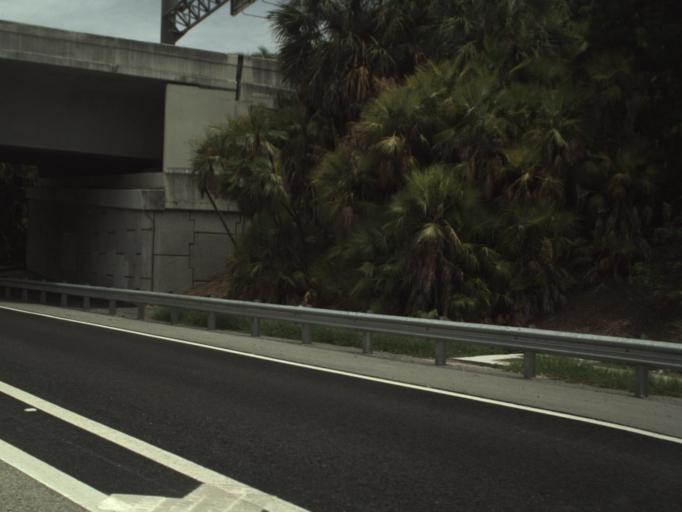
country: US
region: Florida
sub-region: Broward County
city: Dania Beach
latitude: 26.0716
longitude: -80.1339
